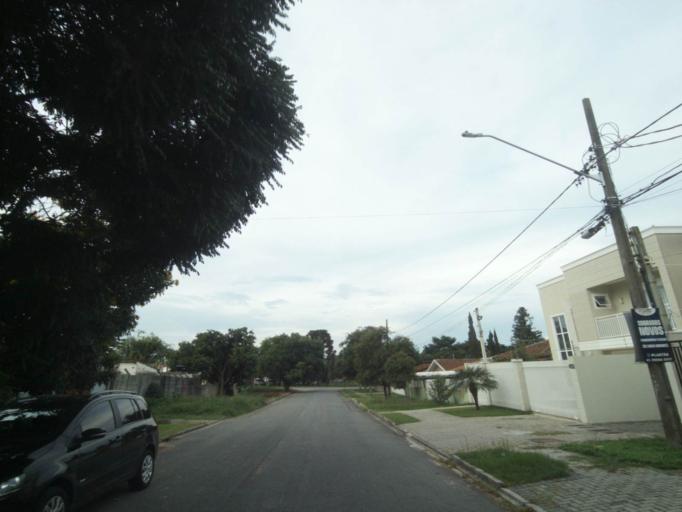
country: BR
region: Parana
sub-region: Pinhais
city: Pinhais
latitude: -25.4419
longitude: -49.2268
